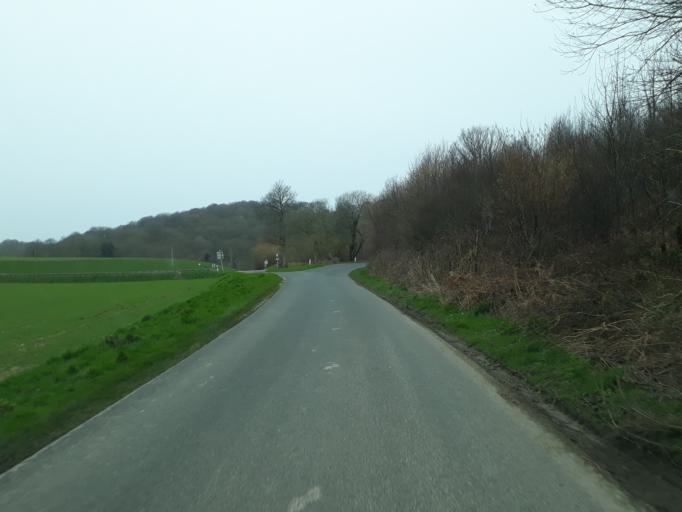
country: FR
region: Haute-Normandie
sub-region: Departement de la Seine-Maritime
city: Les Loges
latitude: 49.6770
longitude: 0.2566
